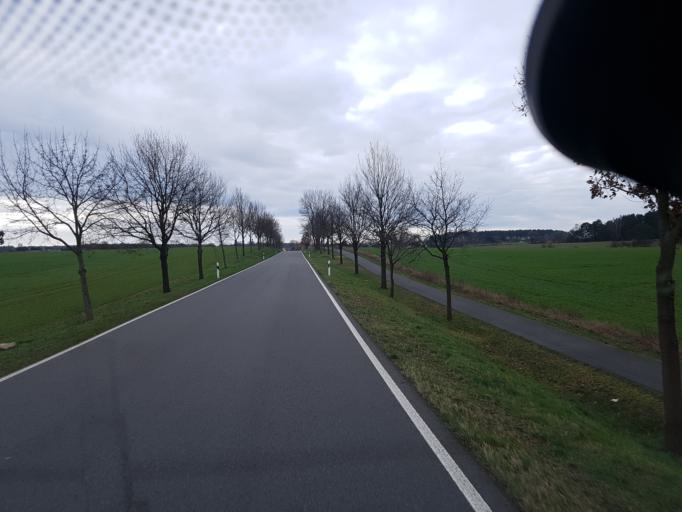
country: DE
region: Brandenburg
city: Gross Lindow
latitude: 52.1507
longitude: 14.5232
